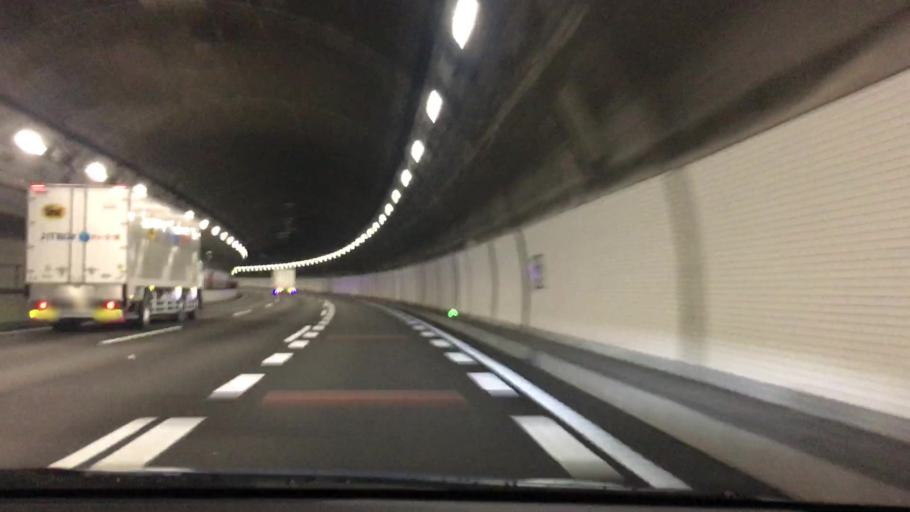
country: JP
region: Shizuoka
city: Gotemba
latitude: 35.3590
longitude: 139.0357
